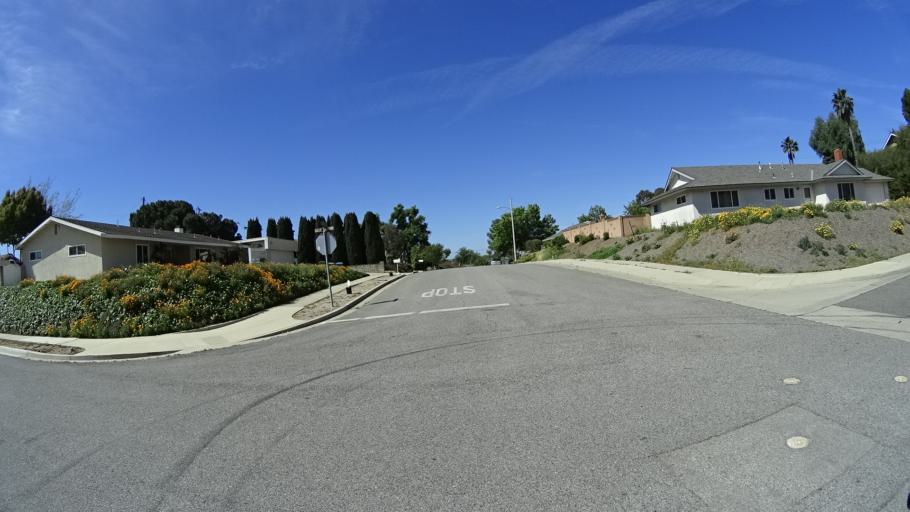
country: US
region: California
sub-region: Ventura County
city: Thousand Oaks
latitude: 34.2208
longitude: -118.8602
